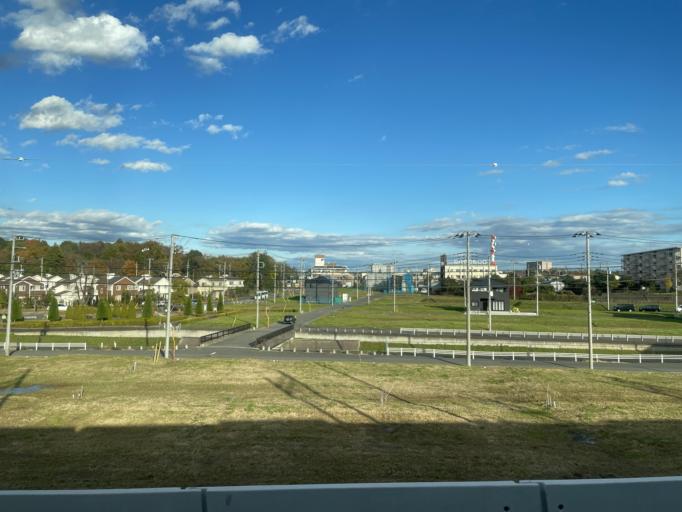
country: JP
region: Chiba
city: Noda
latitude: 35.9553
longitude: 139.8624
